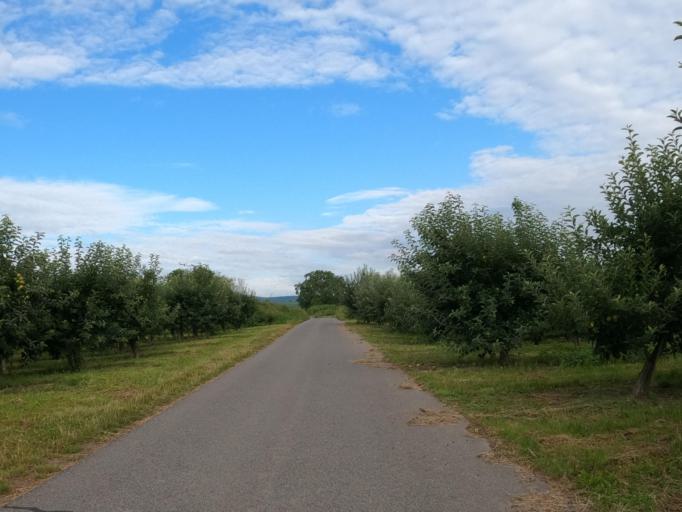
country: DE
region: Rheinland-Pfalz
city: Freinsheim
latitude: 49.5143
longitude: 8.2219
